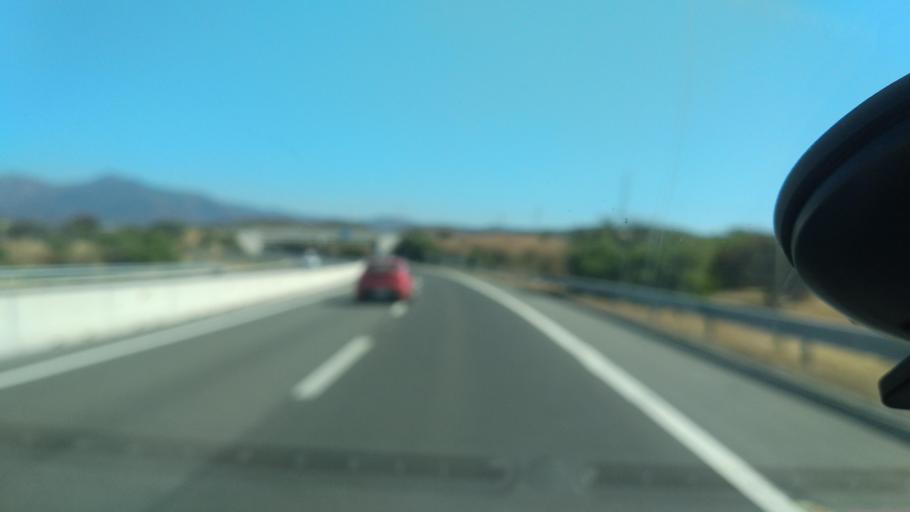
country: CL
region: Valparaiso
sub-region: Provincia de Marga Marga
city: Villa Alemana
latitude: -33.0040
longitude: -71.3286
